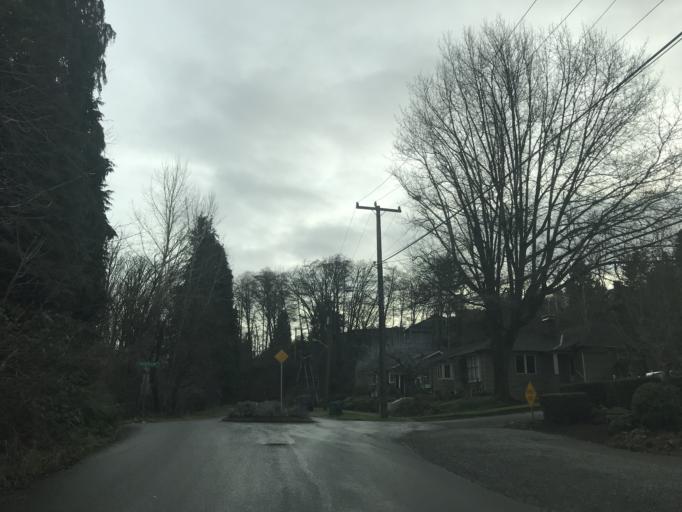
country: US
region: Washington
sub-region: King County
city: Seattle
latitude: 47.6305
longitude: -122.2990
